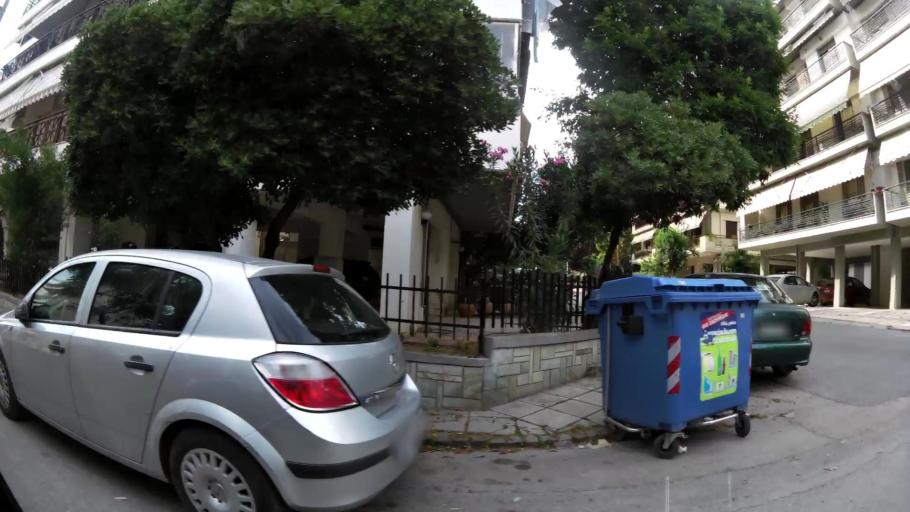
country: GR
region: Central Macedonia
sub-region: Nomos Thessalonikis
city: Kalamaria
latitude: 40.5768
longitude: 22.9513
